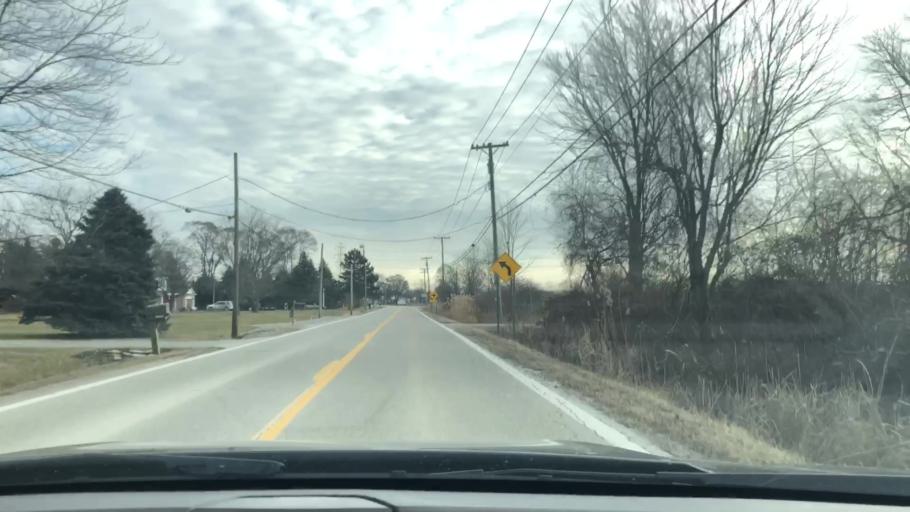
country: US
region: Michigan
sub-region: Macomb County
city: Shelby
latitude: 42.7292
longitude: -83.0000
